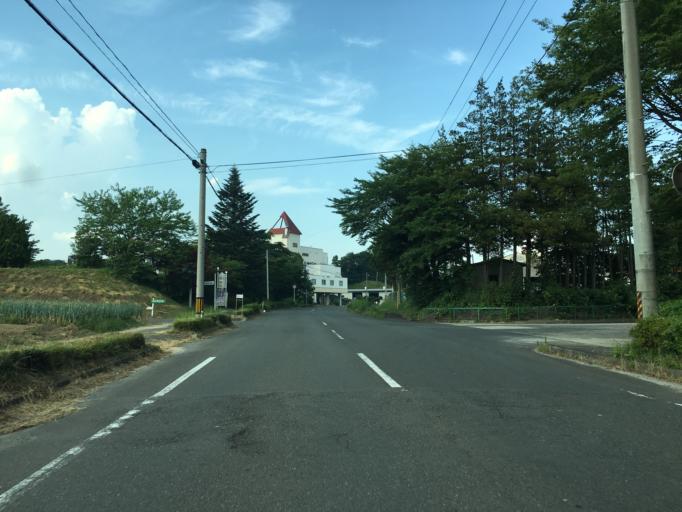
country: JP
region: Fukushima
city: Nihommatsu
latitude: 37.5821
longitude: 140.4377
